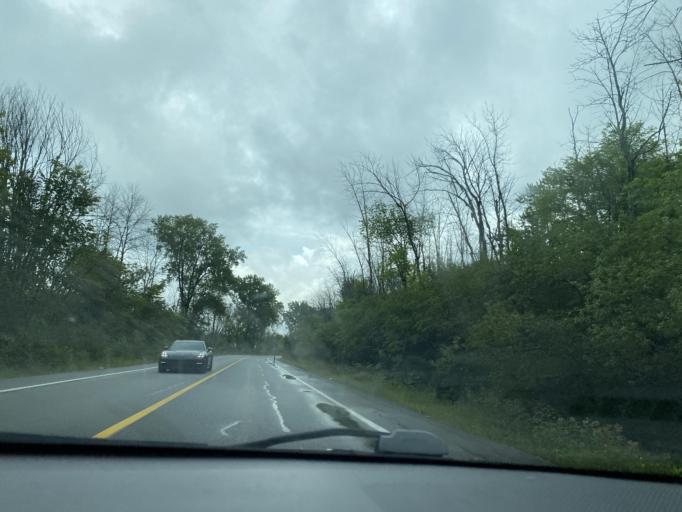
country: CA
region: Quebec
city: Baie-D'Urfe
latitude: 45.4484
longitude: -73.9255
